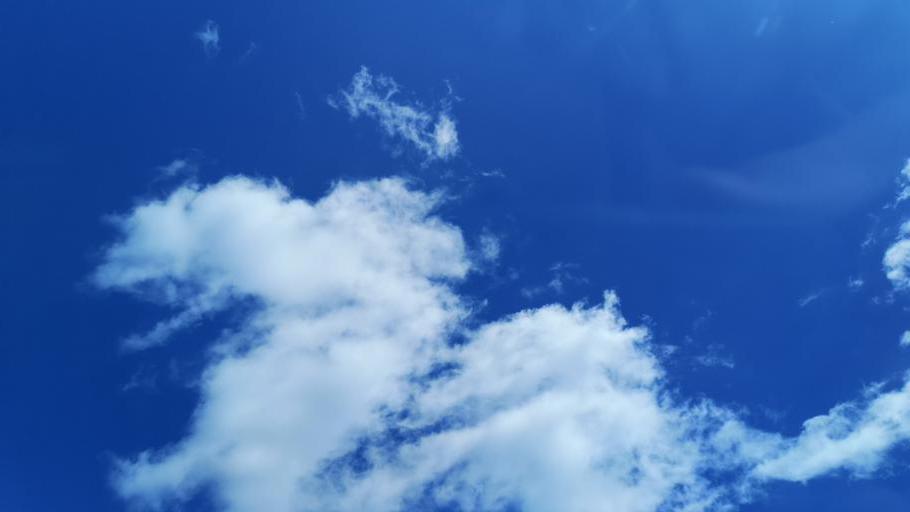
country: DE
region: Baden-Wuerttemberg
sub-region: Regierungsbezirk Stuttgart
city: Altenriet
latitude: 48.5936
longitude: 9.1796
